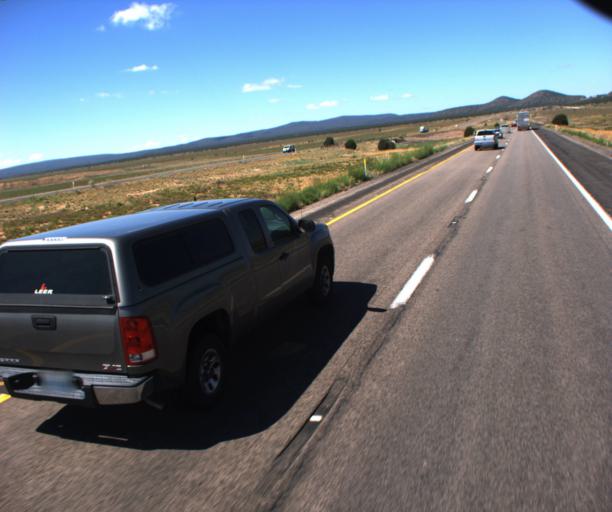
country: US
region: Arizona
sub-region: Mohave County
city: Peach Springs
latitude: 35.3133
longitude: -112.9717
